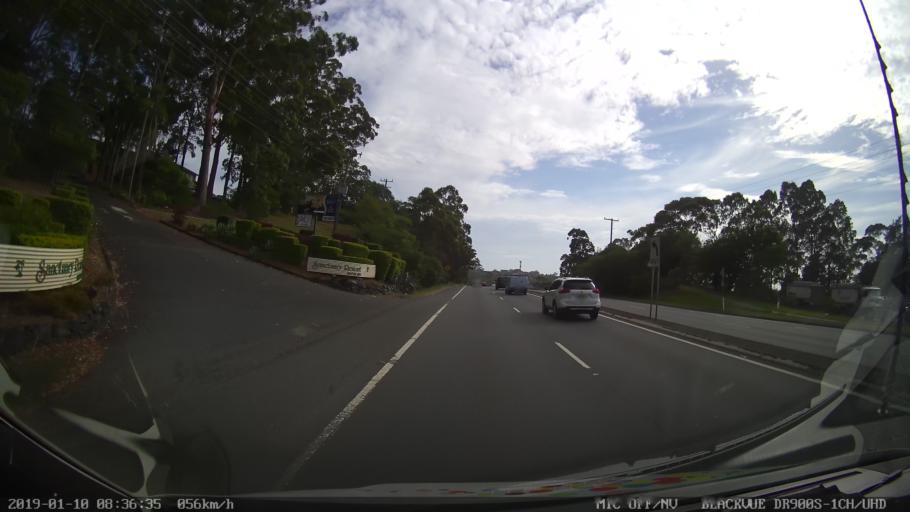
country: AU
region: New South Wales
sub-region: Coffs Harbour
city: Coffs Harbour
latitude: -30.3107
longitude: 153.0975
